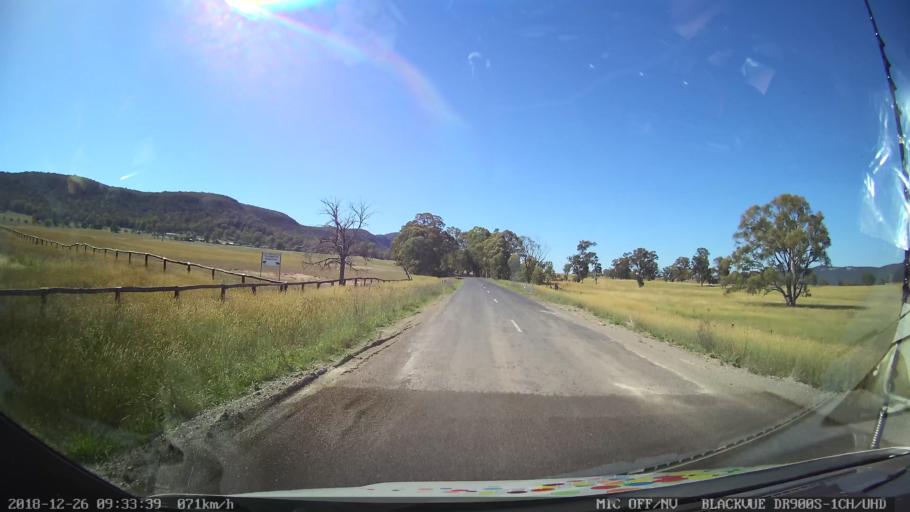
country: AU
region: New South Wales
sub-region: Mid-Western Regional
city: Kandos
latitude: -32.8969
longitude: 150.0355
